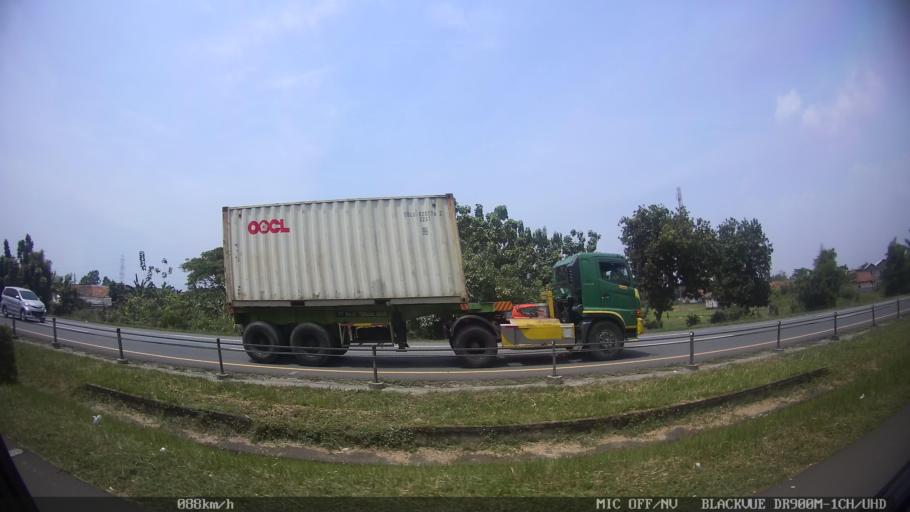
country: ID
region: Banten
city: Serang
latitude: -6.0605
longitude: 106.1228
